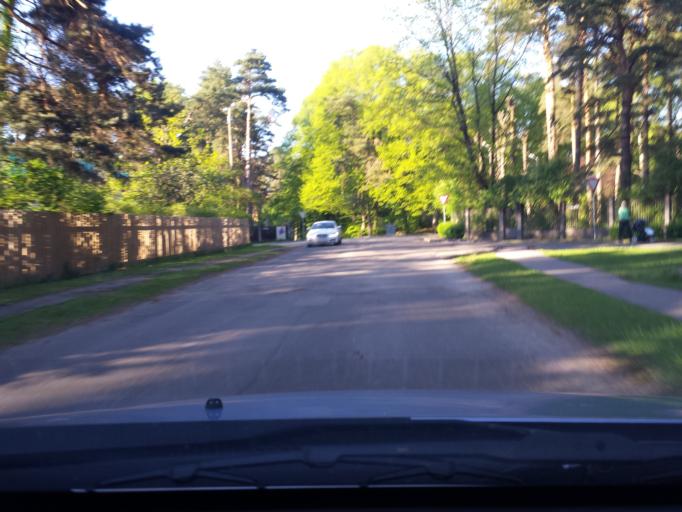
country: LV
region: Riga
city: Jaunciems
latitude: 57.0002
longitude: 24.1646
